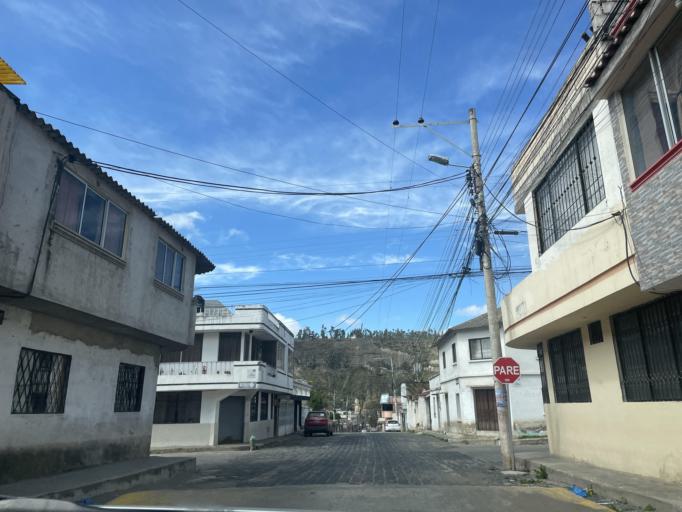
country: EC
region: Chimborazo
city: Guano
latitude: -1.6042
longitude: -78.6444
